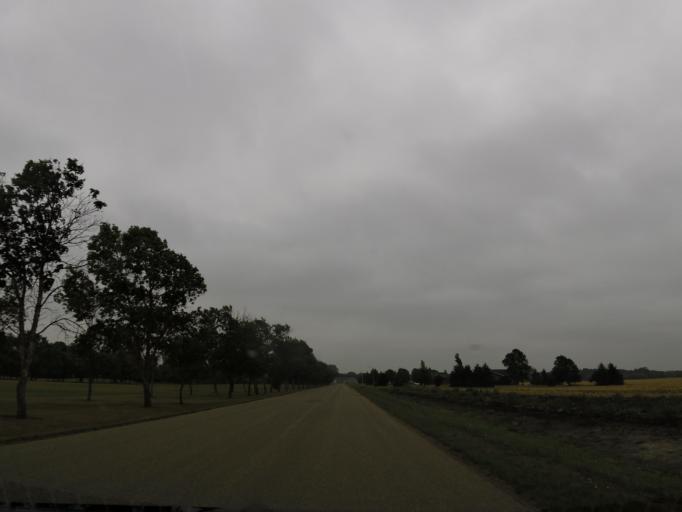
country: US
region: Minnesota
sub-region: Marshall County
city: Warren
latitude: 48.4462
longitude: -96.8882
